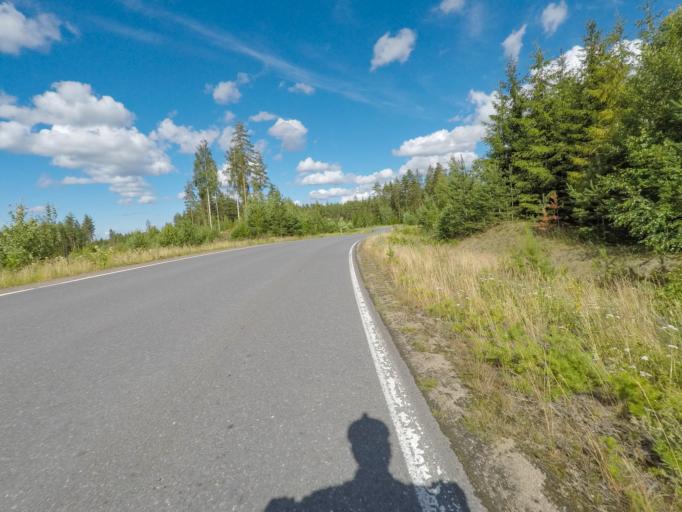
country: FI
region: South Karelia
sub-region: Lappeenranta
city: Joutseno
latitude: 61.0955
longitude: 28.3561
